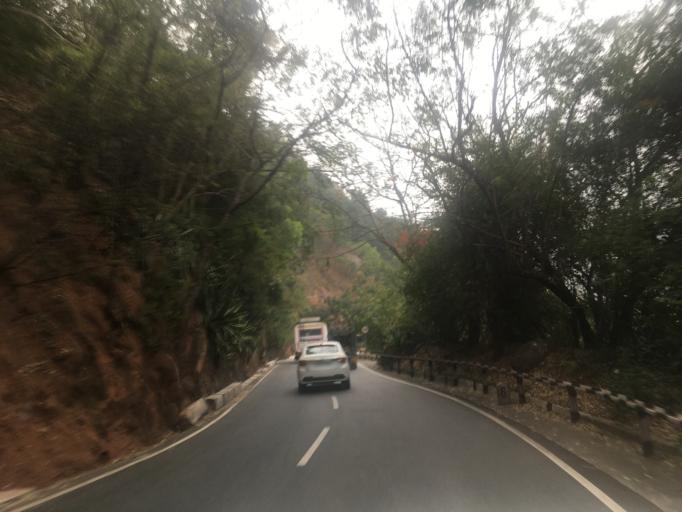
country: IN
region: Andhra Pradesh
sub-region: Chittoor
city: Tirumala
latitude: 13.6679
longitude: 79.3486
